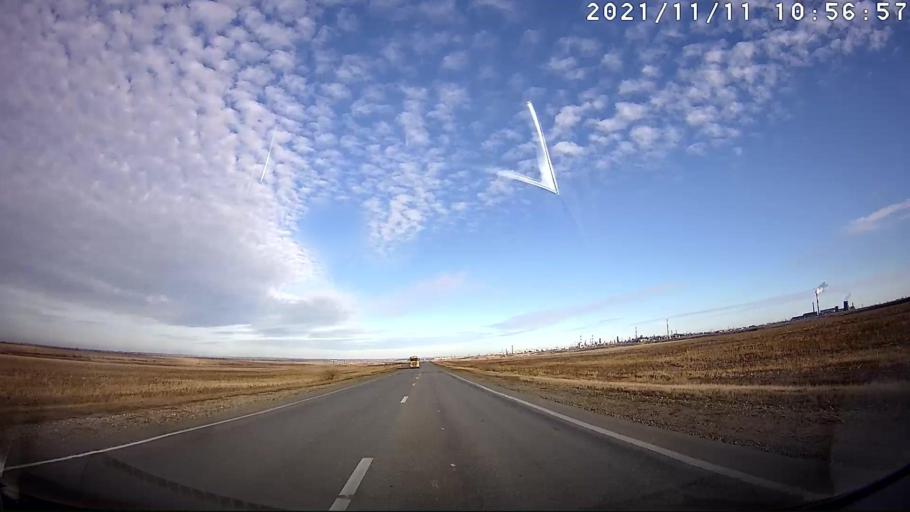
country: RU
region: Samara
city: Varlamovo
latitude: 53.0528
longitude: 48.3463
